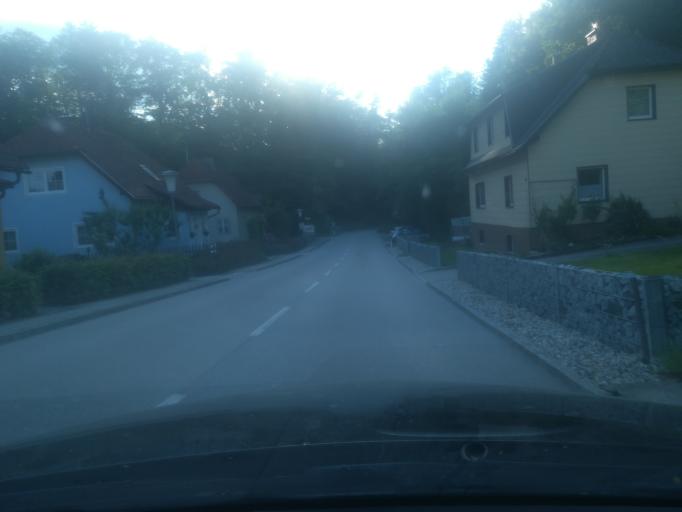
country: AT
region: Upper Austria
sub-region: Politischer Bezirk Perg
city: Perg
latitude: 48.3099
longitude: 14.6154
